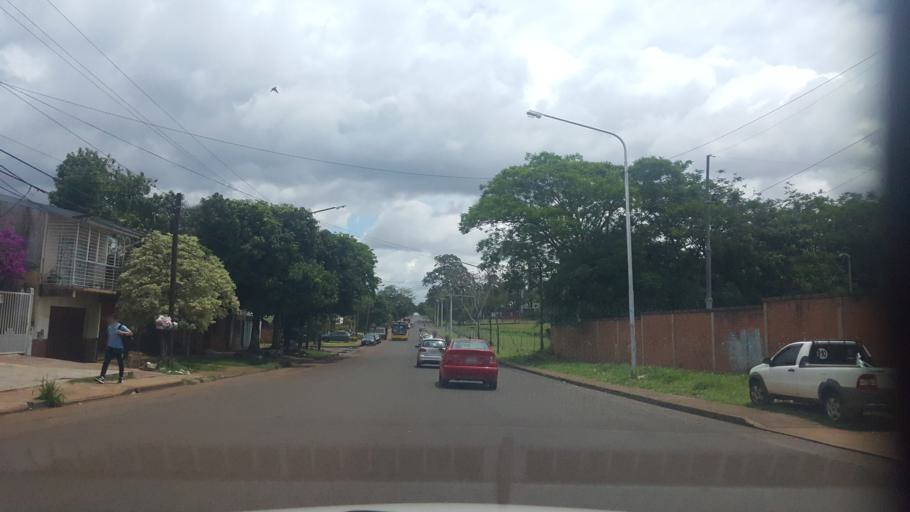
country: AR
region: Misiones
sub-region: Departamento de Capital
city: Posadas
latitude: -27.3660
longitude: -55.9128
